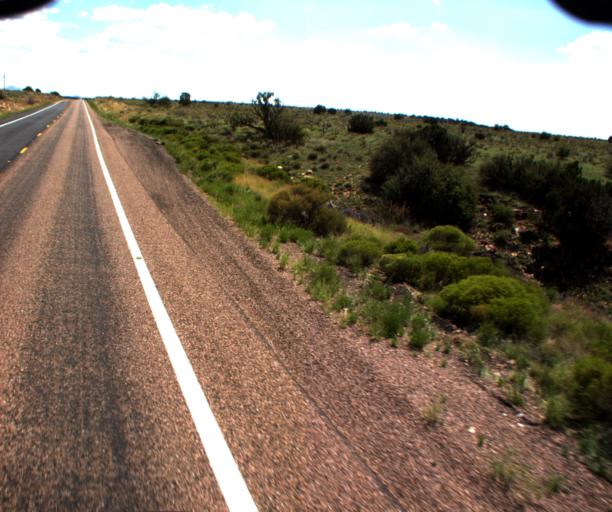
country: US
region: Arizona
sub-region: Coconino County
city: Williams
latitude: 35.5865
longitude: -112.1509
